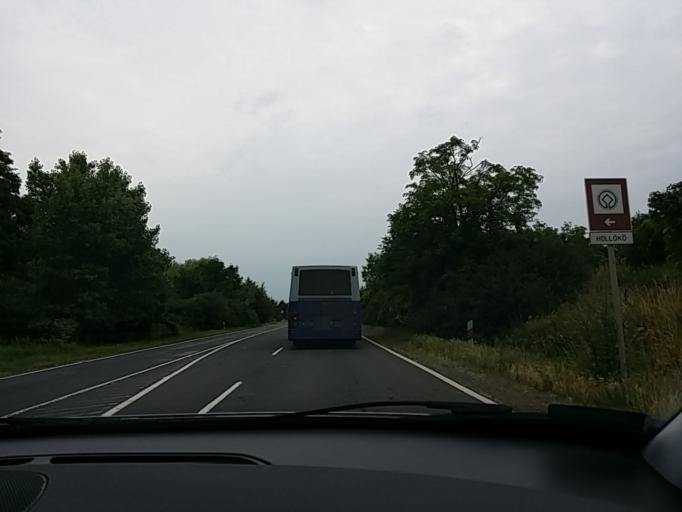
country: HU
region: Nograd
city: Paszto
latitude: 47.8986
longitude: 19.6738
